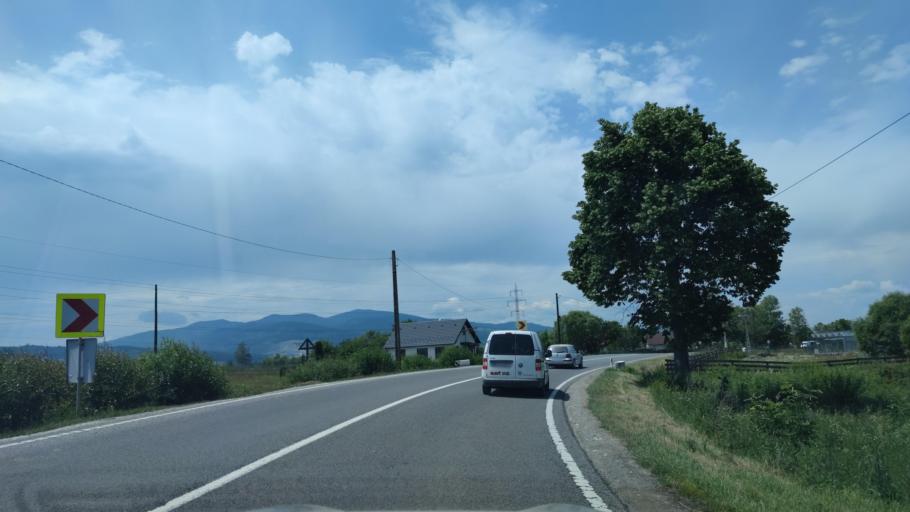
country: RO
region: Harghita
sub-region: Comuna Voslobeni
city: Voslobeni
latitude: 46.6242
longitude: 25.6369
